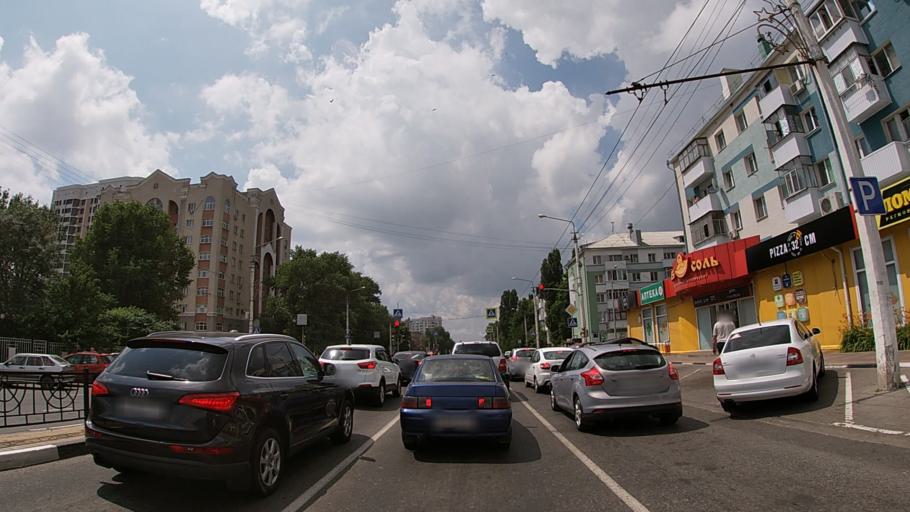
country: RU
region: Belgorod
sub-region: Belgorodskiy Rayon
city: Belgorod
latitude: 50.6124
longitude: 36.5845
